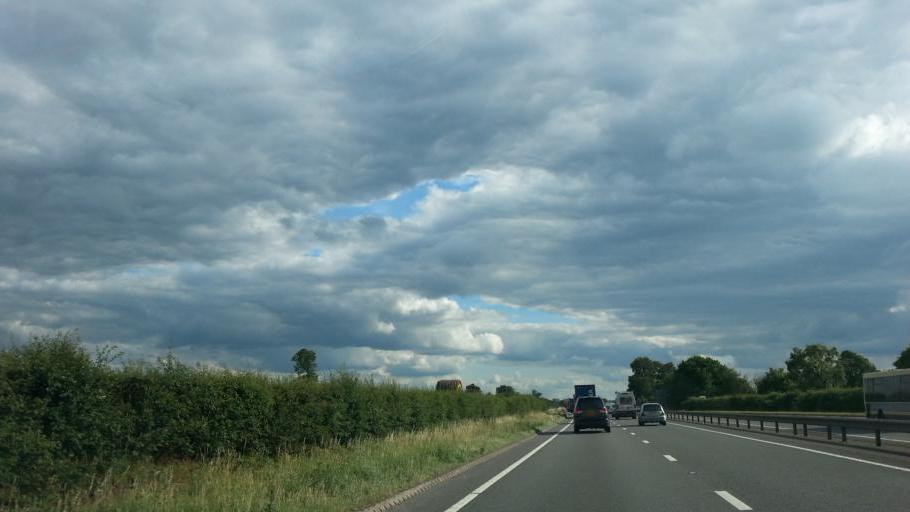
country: GB
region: England
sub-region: Nottinghamshire
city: South Collingham
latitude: 53.1397
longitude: -0.8061
